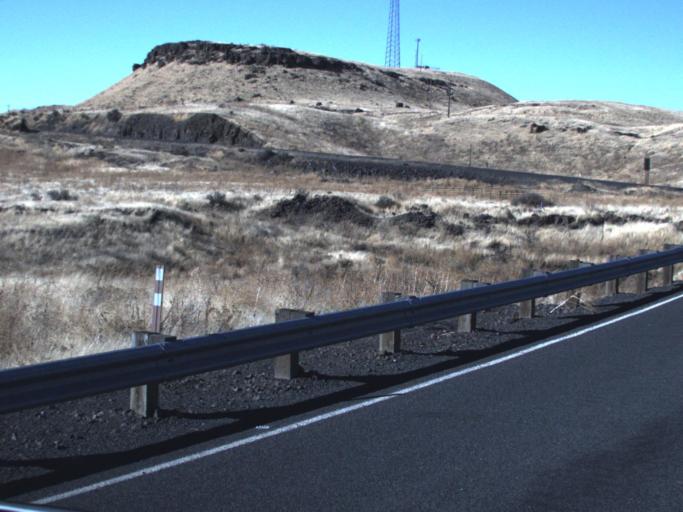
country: US
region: Washington
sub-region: Franklin County
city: Connell
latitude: 46.6341
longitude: -118.5561
